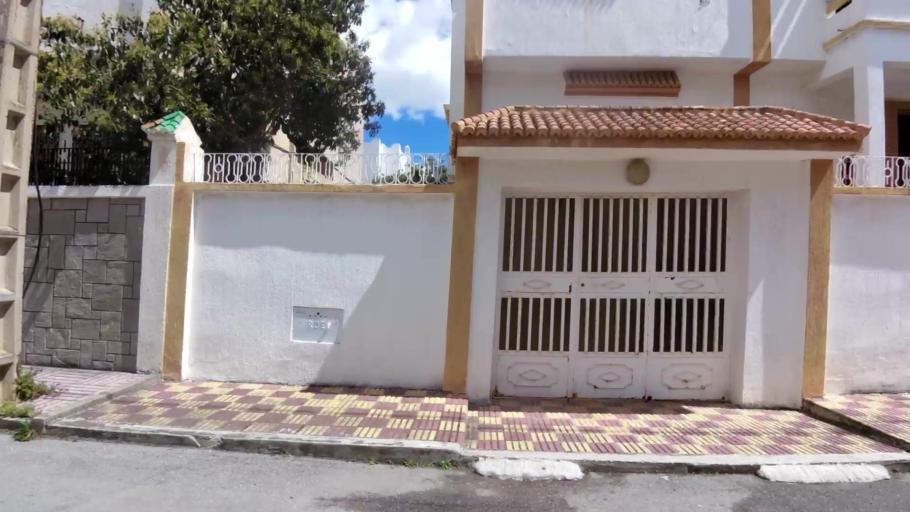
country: MA
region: Tanger-Tetouan
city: Tetouan
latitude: 35.5825
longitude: -5.3465
